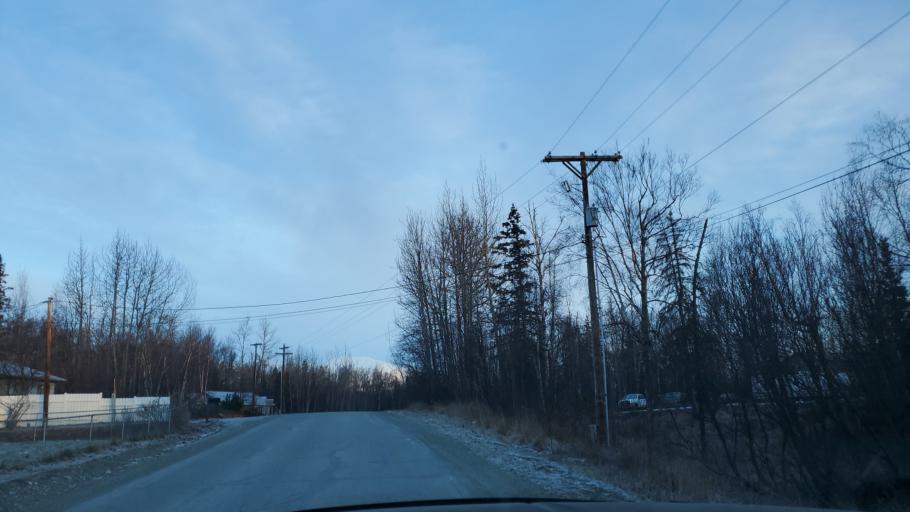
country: US
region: Alaska
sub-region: Matanuska-Susitna Borough
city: Lakes
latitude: 61.6062
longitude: -149.3157
